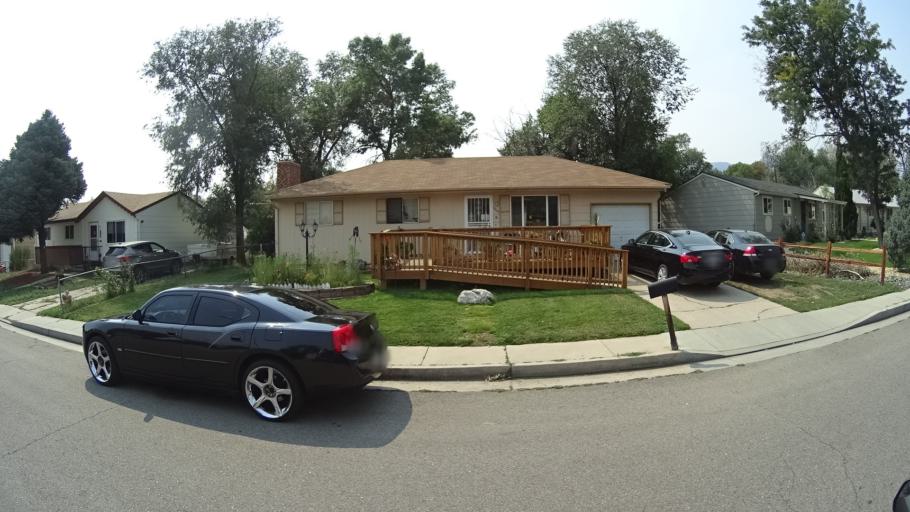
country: US
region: Colorado
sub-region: El Paso County
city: Colorado Springs
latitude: 38.8009
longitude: -104.8128
